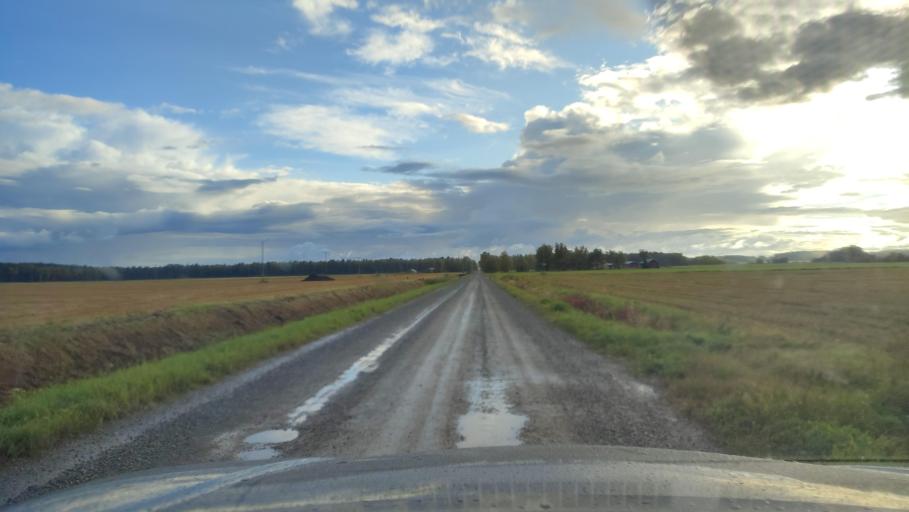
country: FI
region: Southern Ostrobothnia
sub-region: Suupohja
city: Karijoki
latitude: 62.3273
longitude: 21.5773
